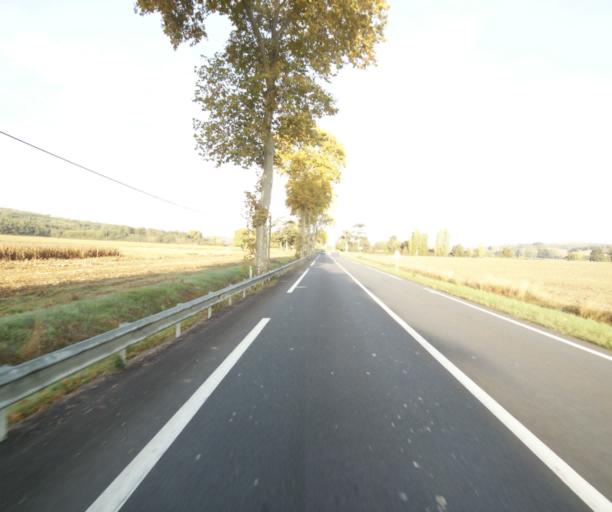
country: FR
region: Midi-Pyrenees
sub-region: Departement du Tarn-et-Garonne
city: Saint-Nauphary
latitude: 43.9432
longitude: 1.4657
